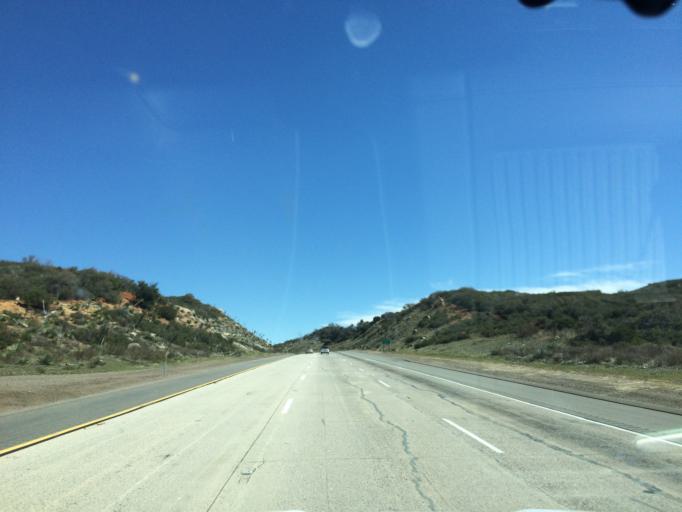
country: US
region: California
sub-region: San Diego County
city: Descanso
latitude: 32.8194
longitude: -116.5869
